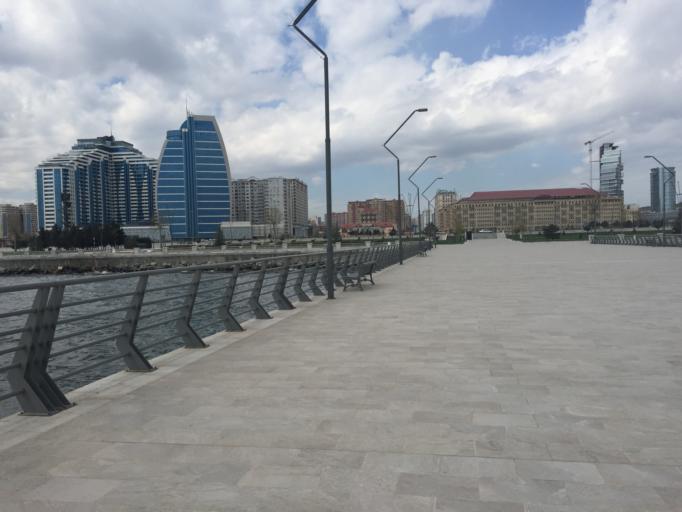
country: AZ
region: Baki
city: Baku
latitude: 40.3739
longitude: 49.8783
